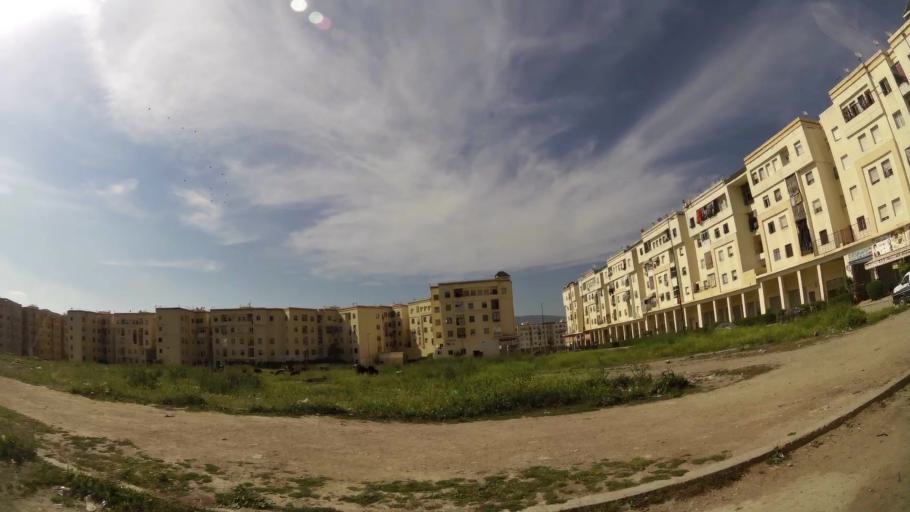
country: MA
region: Fes-Boulemane
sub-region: Fes
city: Fes
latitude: 34.0130
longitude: -5.0407
